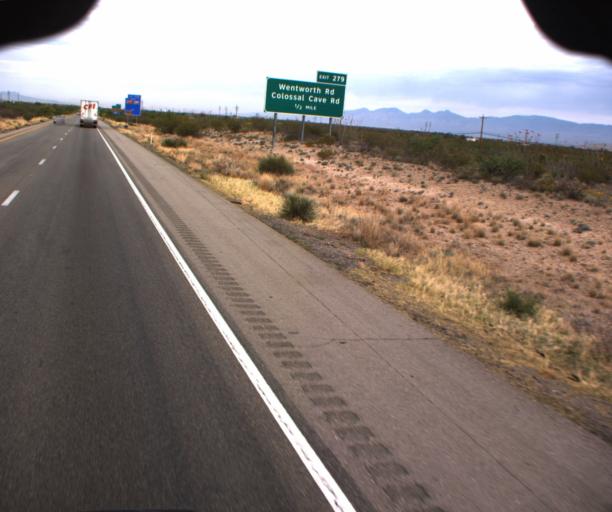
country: US
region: Arizona
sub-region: Pima County
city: Vail
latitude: 32.0199
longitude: -110.7087
